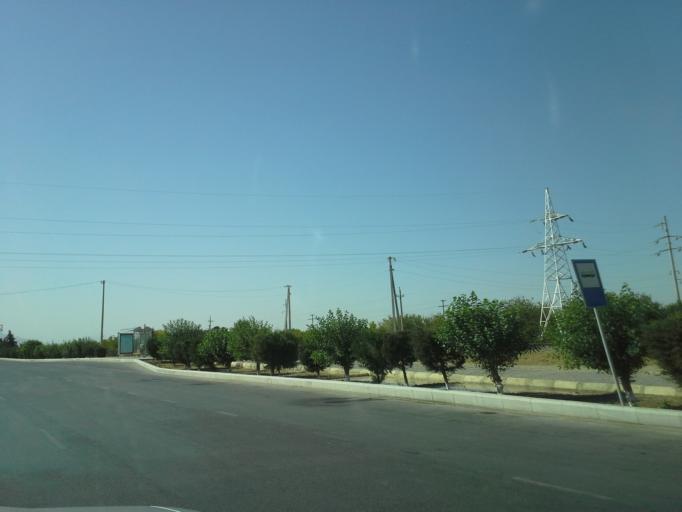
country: TM
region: Ahal
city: Annau
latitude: 37.9166
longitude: 58.4688
